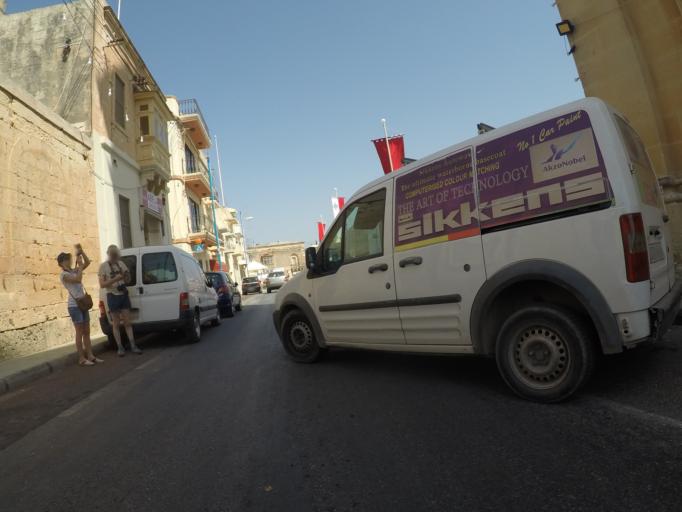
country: MT
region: L-Imgarr
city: Imgarr
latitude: 35.9197
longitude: 14.3664
